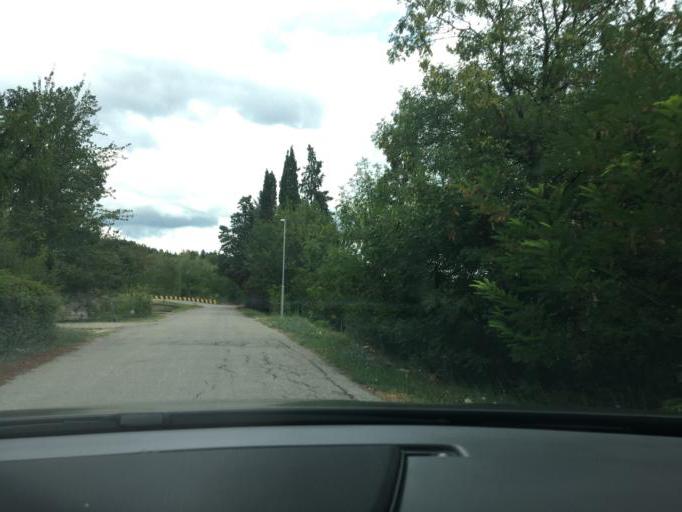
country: MK
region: Cair
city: Cair
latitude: 42.0010
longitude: 21.4525
